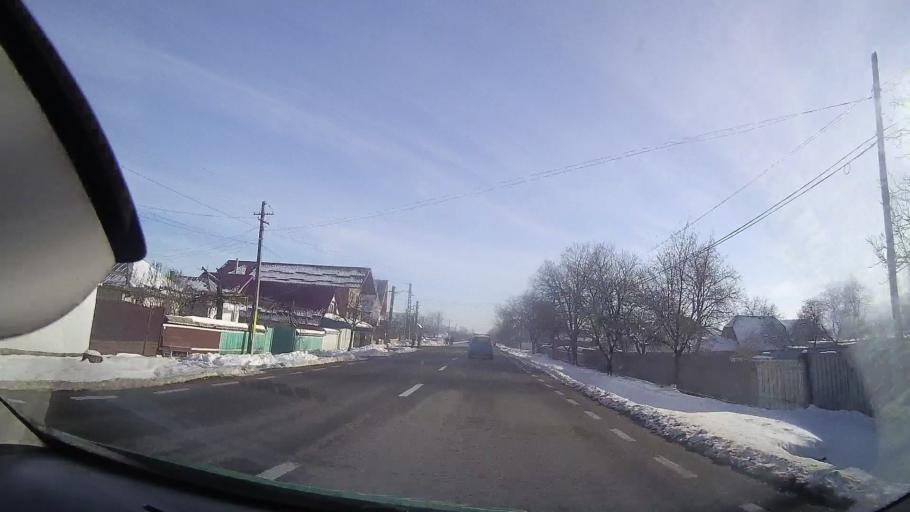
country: RO
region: Neamt
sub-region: Comuna Negresti
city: Negresti
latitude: 47.0556
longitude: 26.3948
